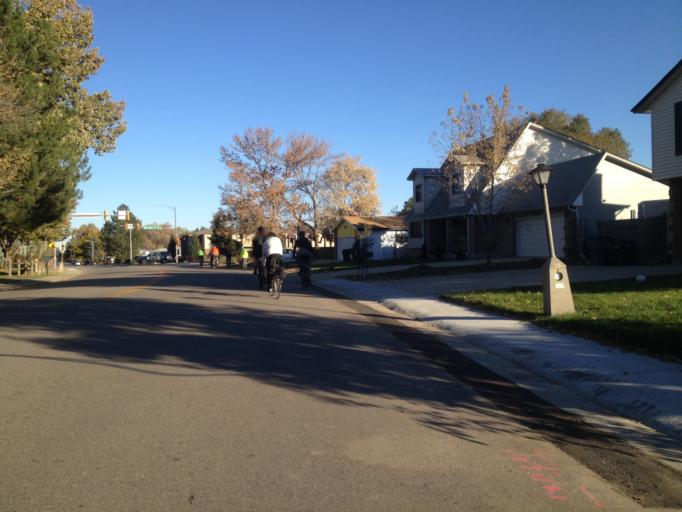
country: US
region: Colorado
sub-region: Boulder County
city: Longmont
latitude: 40.1850
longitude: -105.1320
